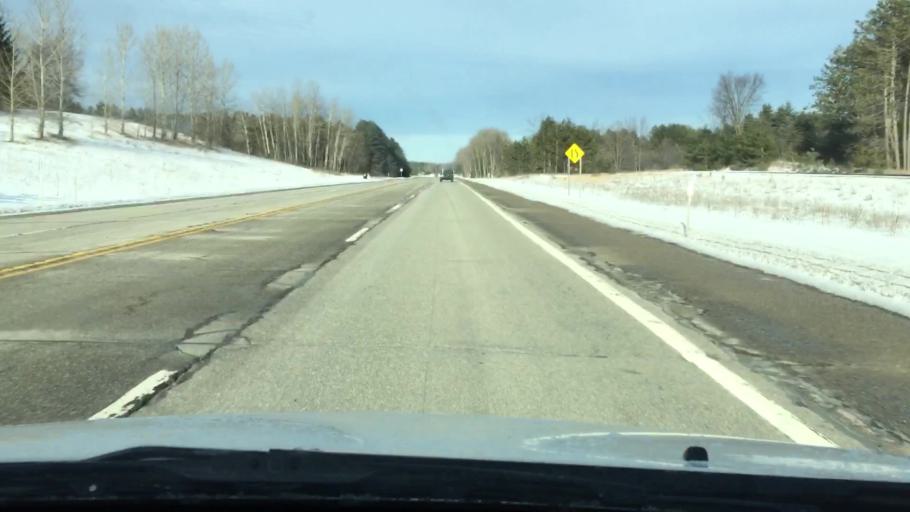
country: US
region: Michigan
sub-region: Kalkaska County
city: Kalkaska
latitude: 44.6212
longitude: -85.2995
